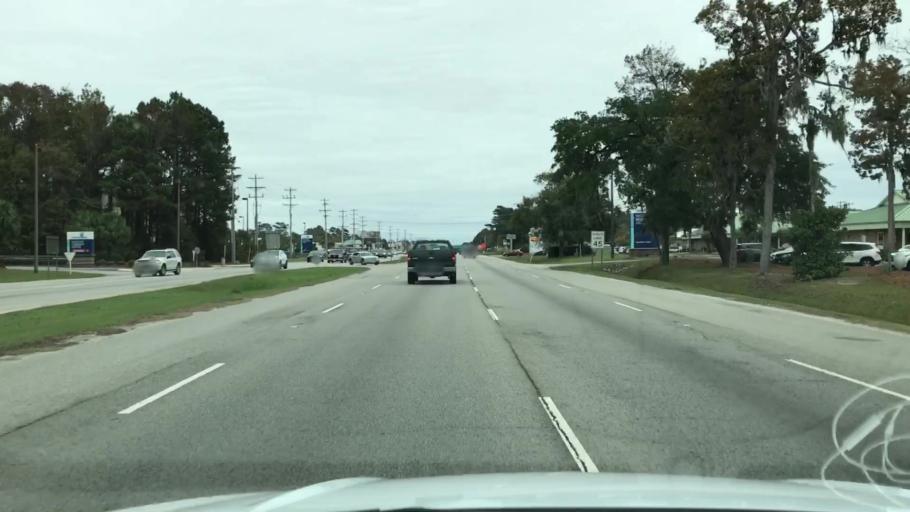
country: US
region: South Carolina
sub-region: Georgetown County
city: Murrells Inlet
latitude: 33.5594
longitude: -79.0413
